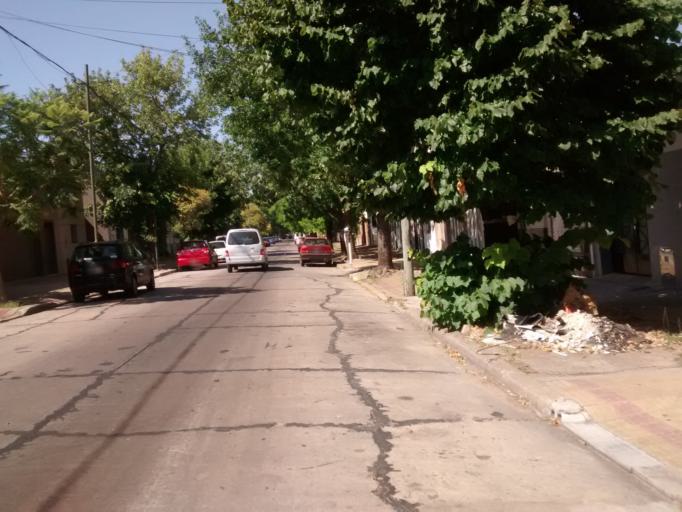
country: AR
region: Buenos Aires
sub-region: Partido de La Plata
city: La Plata
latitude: -34.9057
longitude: -57.9703
